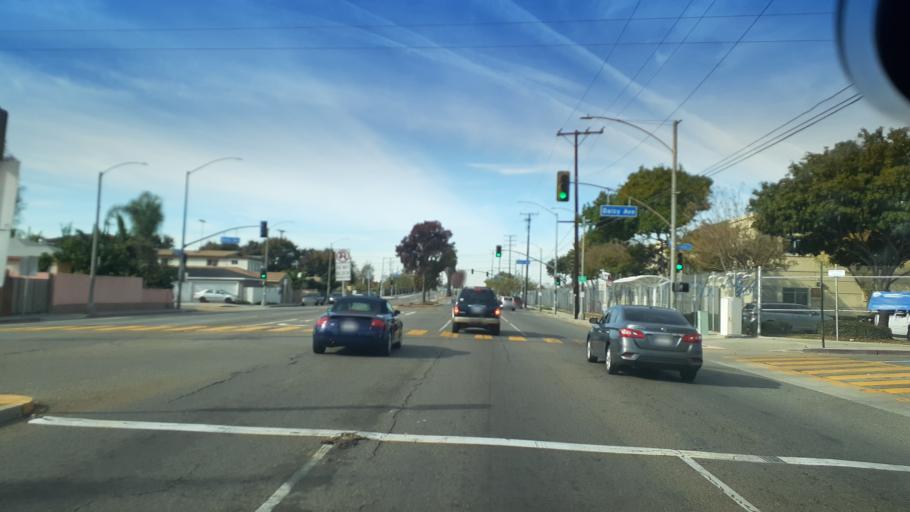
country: US
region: California
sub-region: Los Angeles County
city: East Rancho Dominguez
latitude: 33.8467
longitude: -118.1984
